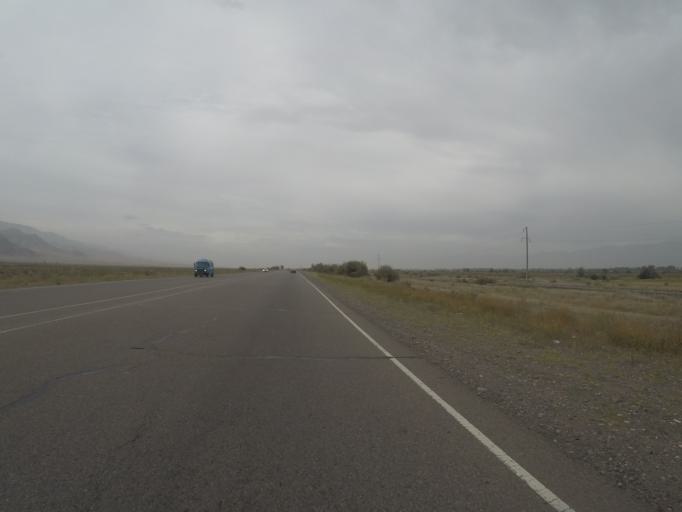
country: KG
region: Chuy
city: Tokmok
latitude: 42.8298
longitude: 75.4669
